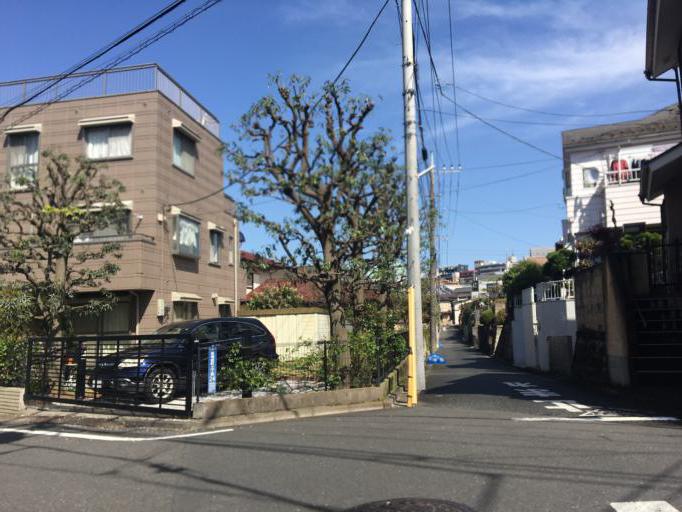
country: JP
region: Saitama
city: Wako
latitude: 35.7717
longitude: 139.6337
